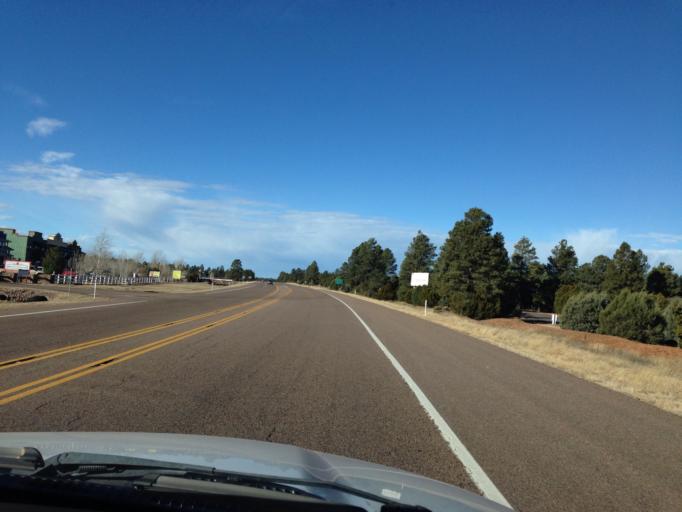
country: US
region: Arizona
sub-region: Navajo County
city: Linden
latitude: 34.3442
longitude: -110.2907
